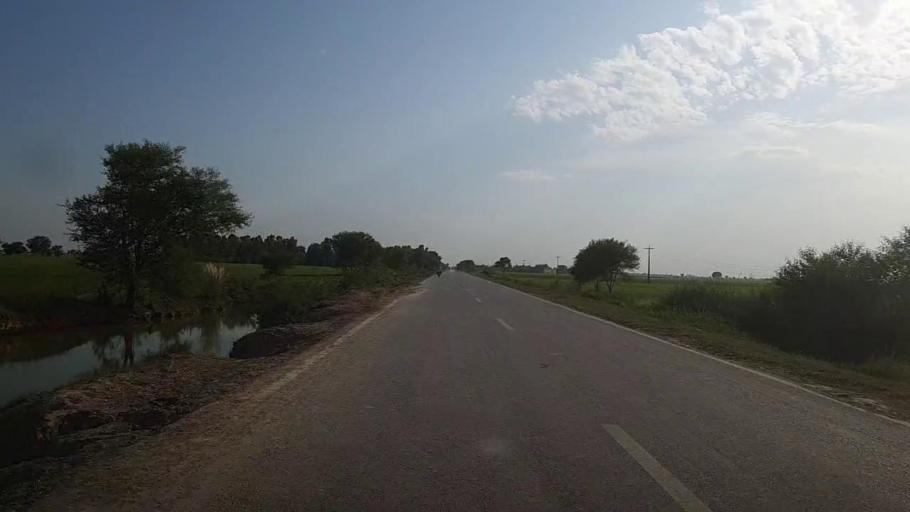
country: PK
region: Sindh
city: Thul
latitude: 28.2242
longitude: 68.7611
